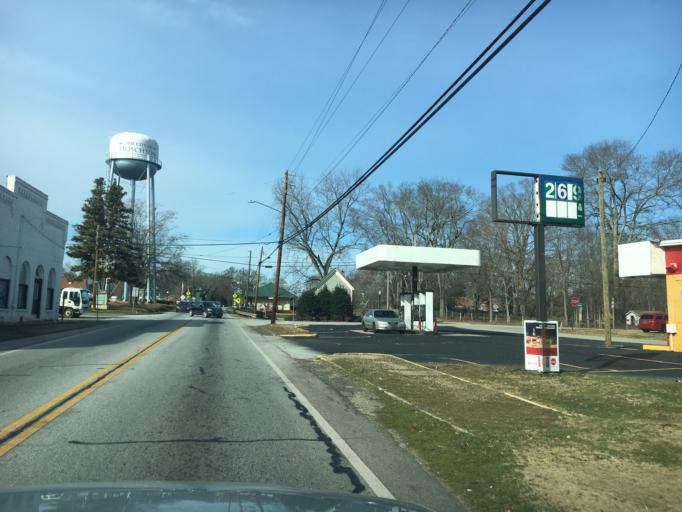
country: US
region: Georgia
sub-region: Jackson County
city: Hoschton
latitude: 34.0962
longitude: -83.7613
